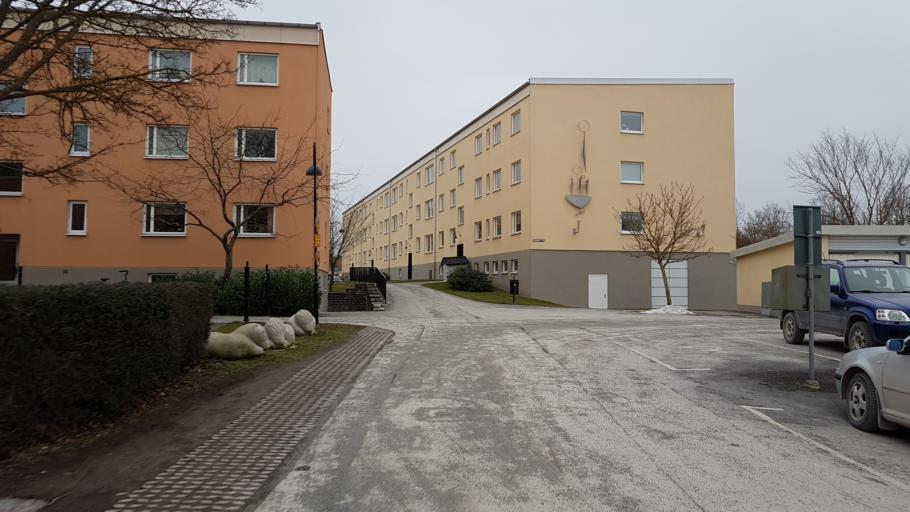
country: SE
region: Gotland
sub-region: Gotland
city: Visby
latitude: 57.6371
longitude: 18.3148
